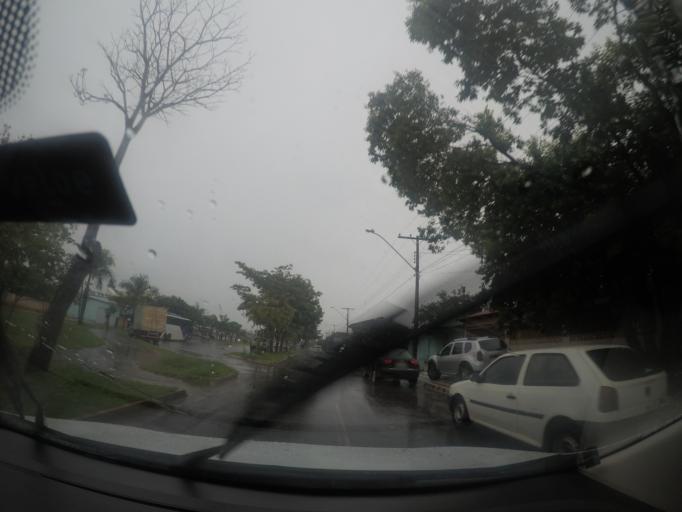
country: BR
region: Goias
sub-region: Goiania
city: Goiania
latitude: -16.6123
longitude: -49.3444
